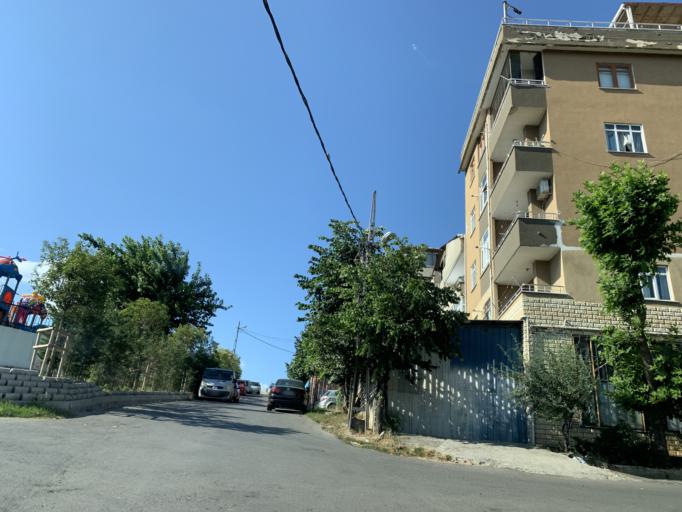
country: TR
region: Istanbul
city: Pendik
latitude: 40.8821
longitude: 29.2599
